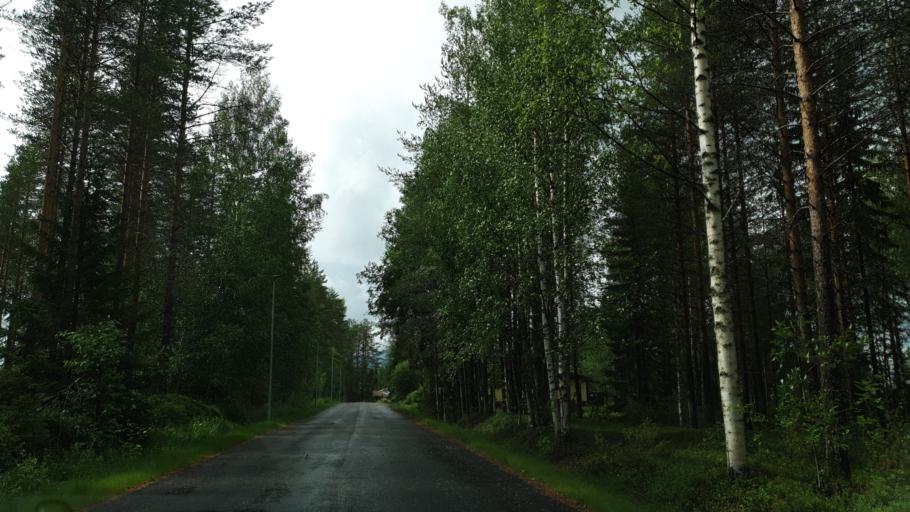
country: FI
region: Kainuu
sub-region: Kehys-Kainuu
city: Kuhmo
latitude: 64.1160
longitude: 29.5105
